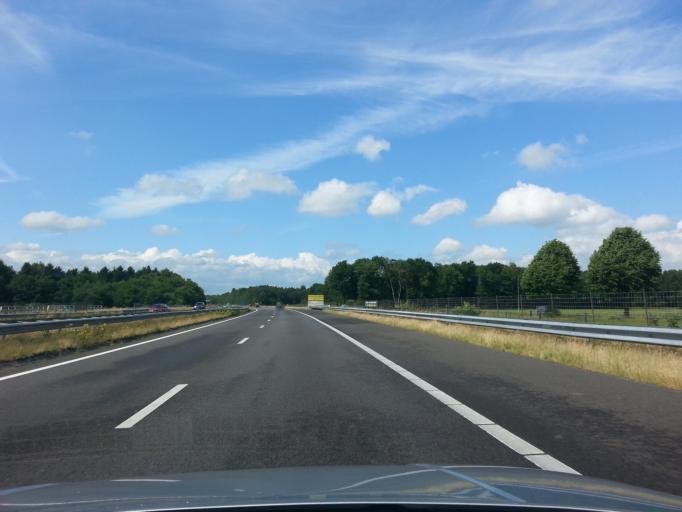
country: NL
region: Limburg
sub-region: Gemeente Venray
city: Venray
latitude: 51.5655
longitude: 5.9941
